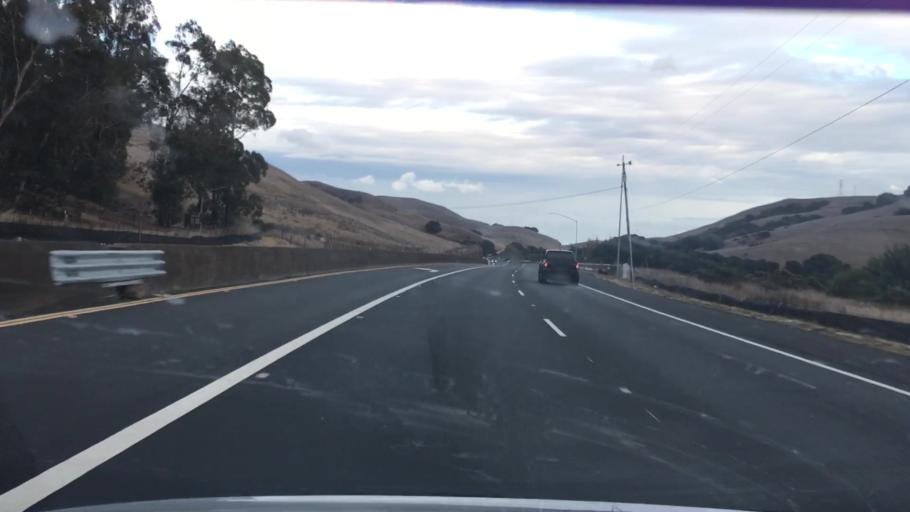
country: US
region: California
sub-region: Solano County
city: Green Valley
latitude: 38.2089
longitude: -122.1948
